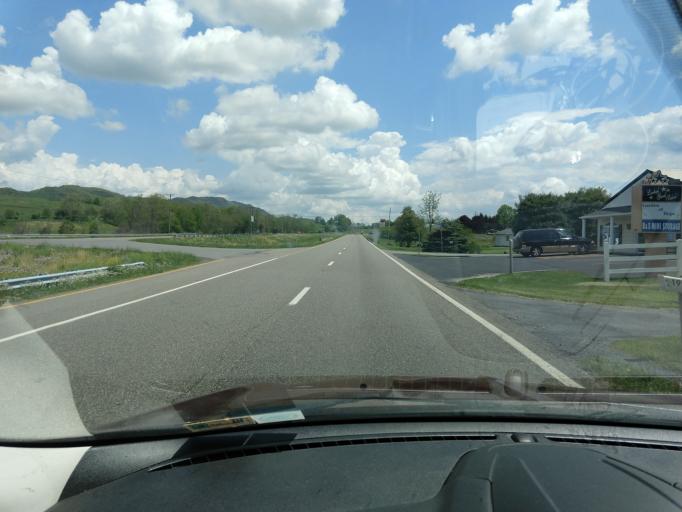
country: US
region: Virginia
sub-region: Russell County
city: Honaker
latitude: 36.9636
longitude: -81.9223
